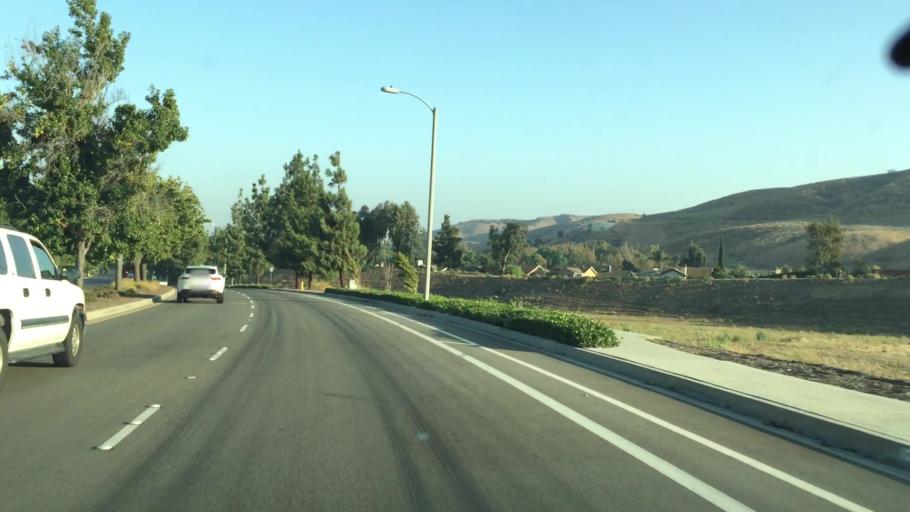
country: US
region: California
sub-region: San Bernardino County
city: Los Serranos
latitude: 33.9372
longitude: -117.6768
